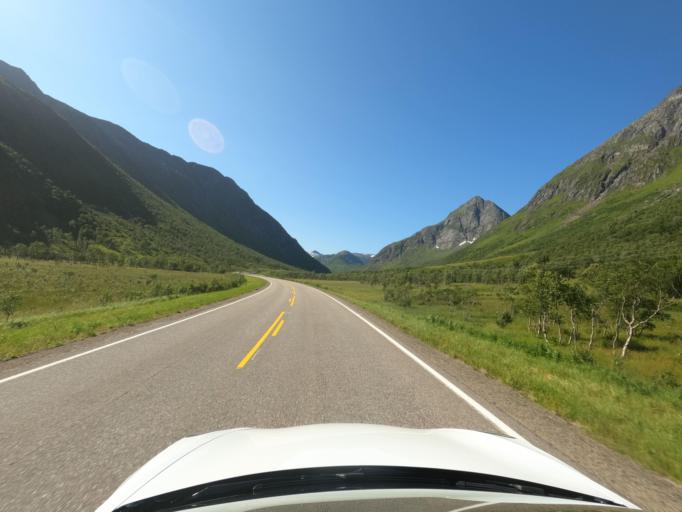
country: NO
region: Nordland
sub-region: Lodingen
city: Lodingen
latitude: 68.5144
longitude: 15.7378
